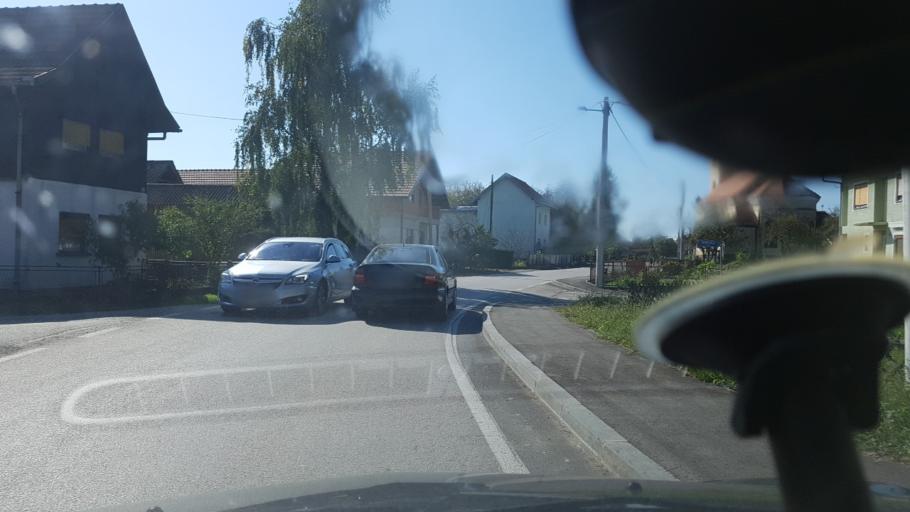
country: HR
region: Zagrebacka
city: Lupoglav
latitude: 45.7371
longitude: 16.3011
